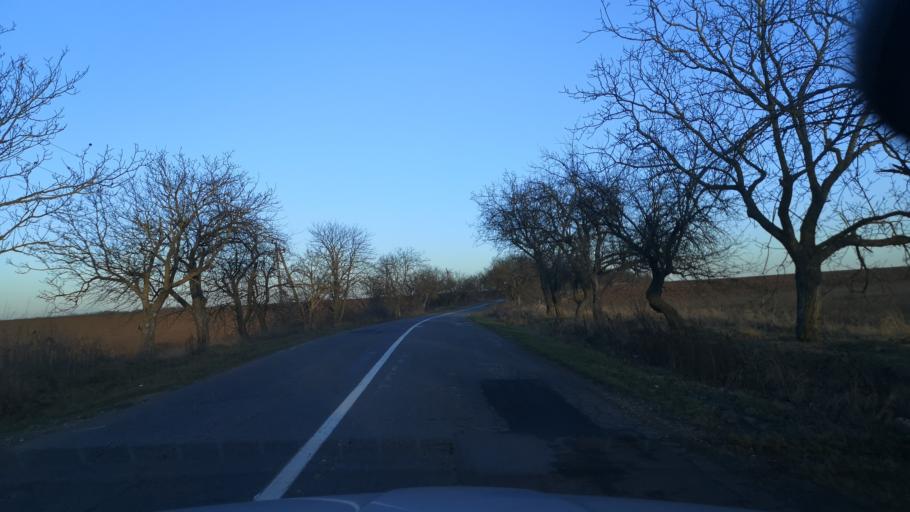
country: MD
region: Orhei
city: Orhei
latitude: 47.3109
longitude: 28.9430
